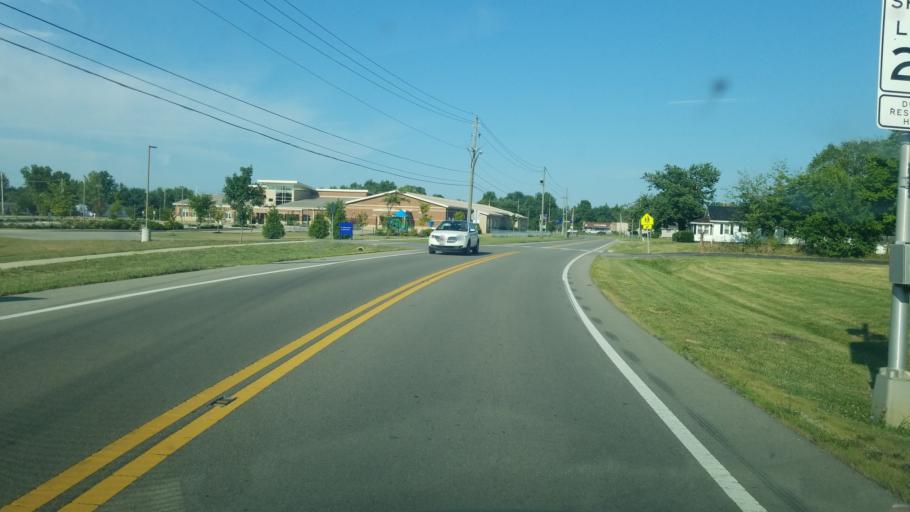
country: US
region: Ohio
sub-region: Franklin County
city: Grove City
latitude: 39.8547
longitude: -83.1847
